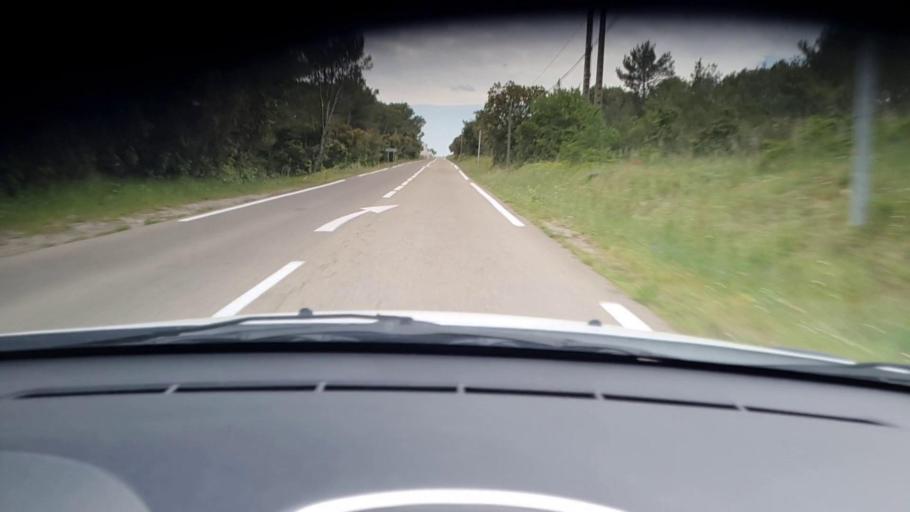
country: FR
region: Languedoc-Roussillon
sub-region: Departement du Gard
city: Poulx
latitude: 43.8802
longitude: 4.3794
